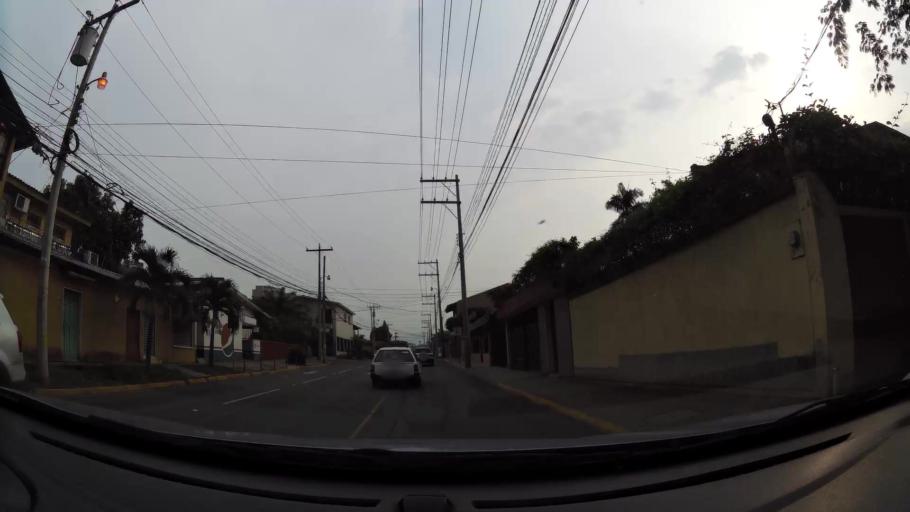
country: HN
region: Francisco Morazan
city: Tegucigalpa
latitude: 14.0838
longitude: -87.1997
